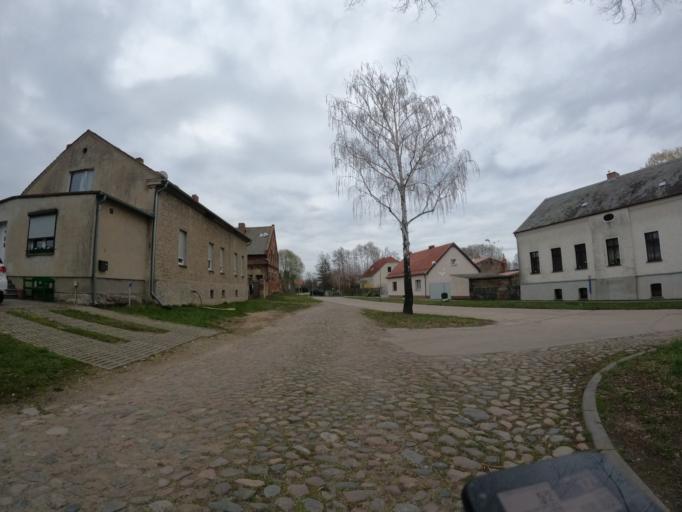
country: DE
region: Brandenburg
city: Petershagen
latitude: 52.5866
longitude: 13.7910
